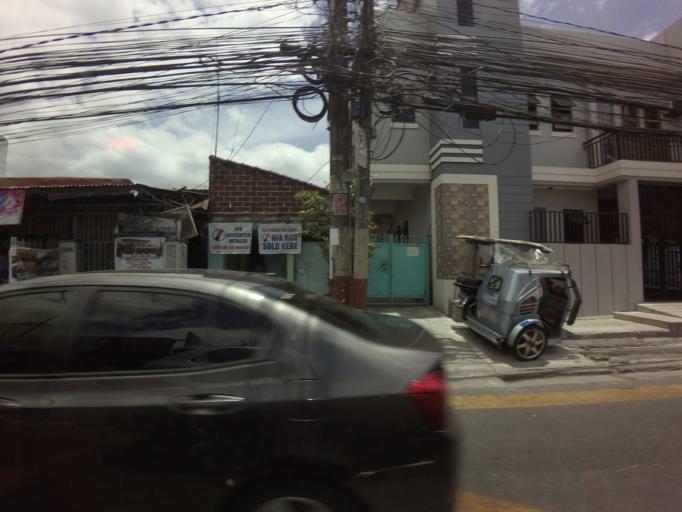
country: PH
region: Metro Manila
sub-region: Marikina
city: Calumpang
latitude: 14.6032
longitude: 121.0981
